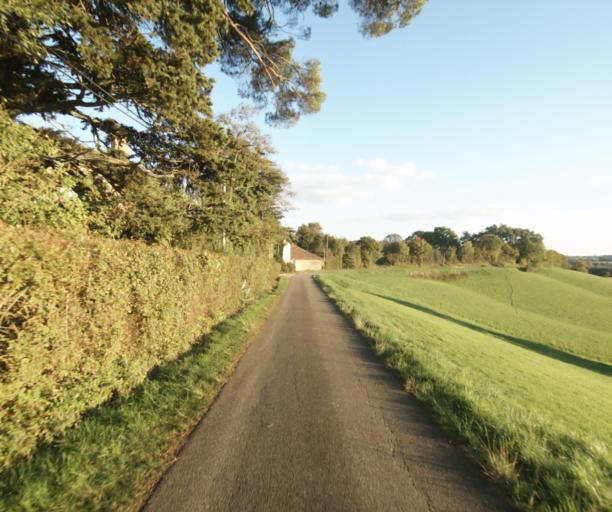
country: FR
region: Midi-Pyrenees
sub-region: Departement du Gers
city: Eauze
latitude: 43.7560
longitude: 0.1662
